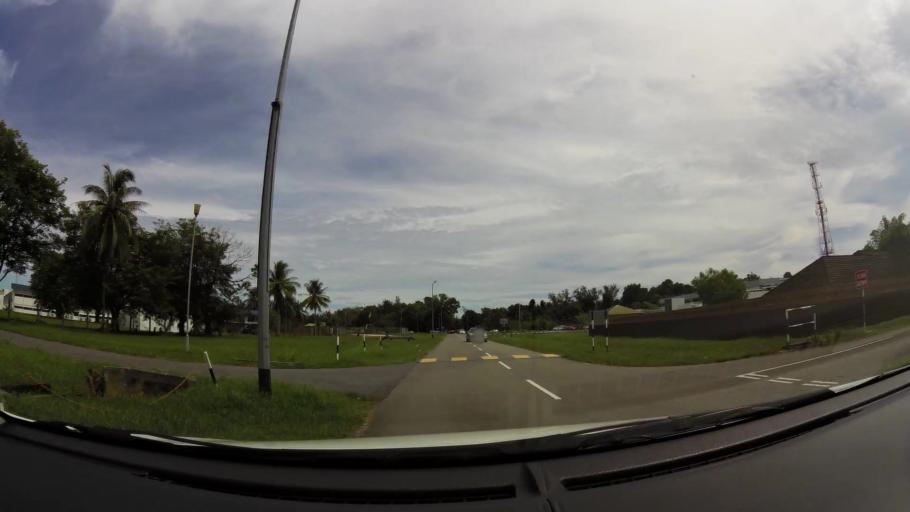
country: BN
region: Belait
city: Seria
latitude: 4.5991
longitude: 114.2866
